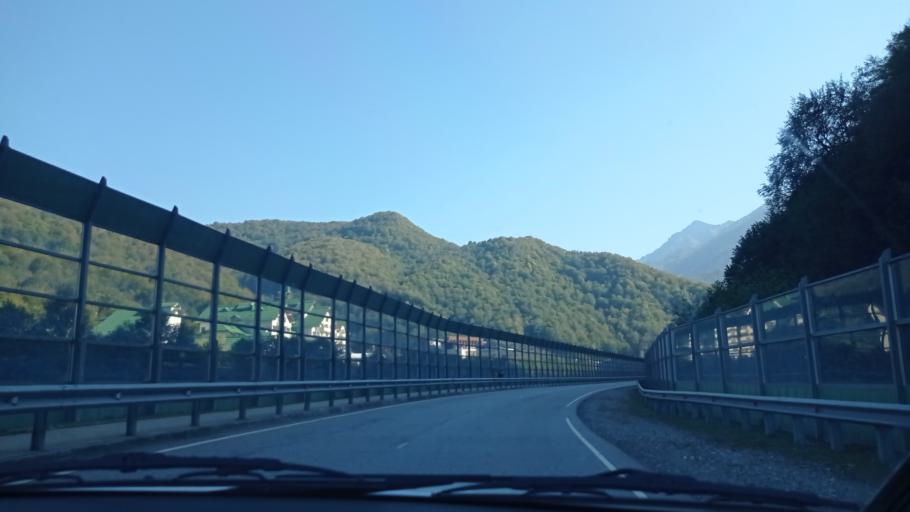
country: RU
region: Krasnodarskiy
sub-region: Sochi City
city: Krasnaya Polyana
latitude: 43.6902
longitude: 40.2732
